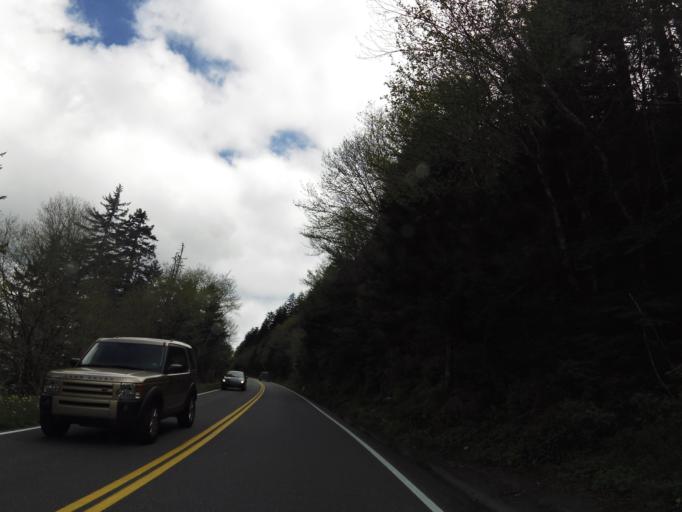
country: US
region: North Carolina
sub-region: Swain County
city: Bryson City
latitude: 35.5642
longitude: -83.4943
